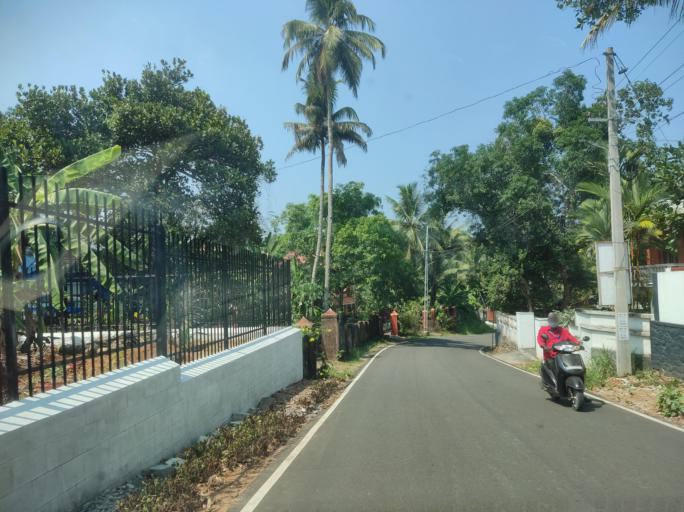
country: IN
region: Kerala
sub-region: Pattanamtitta
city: Adur
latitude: 9.1515
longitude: 76.7244
